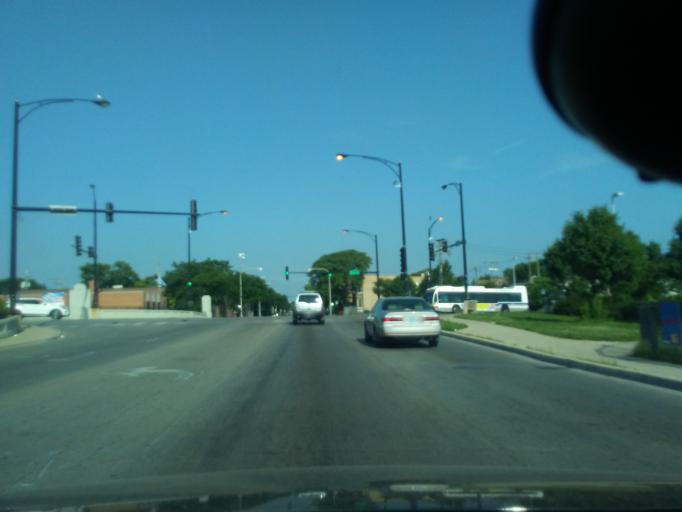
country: US
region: Illinois
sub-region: Cook County
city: Oak Park
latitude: 41.9186
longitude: -87.7651
